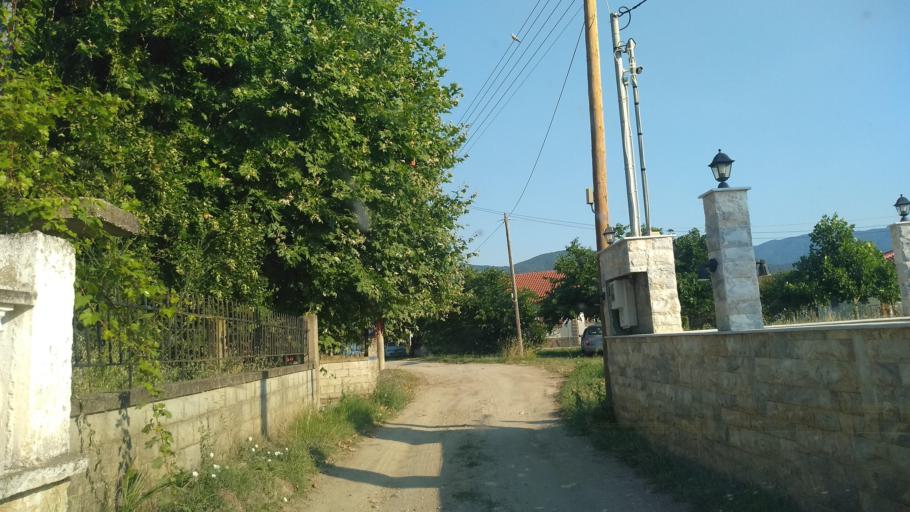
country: GR
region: Central Macedonia
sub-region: Nomos Thessalonikis
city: Nea Vrasna
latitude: 40.6860
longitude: 23.6857
